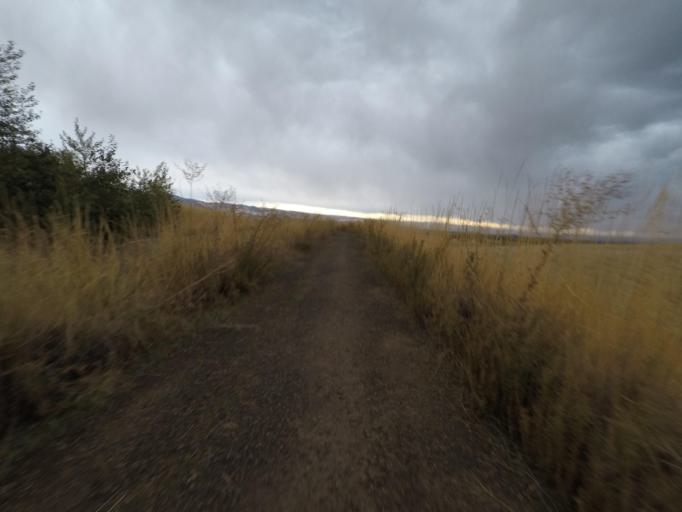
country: US
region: Washington
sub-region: Walla Walla County
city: Walla Walla East
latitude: 46.0635
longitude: -118.2684
